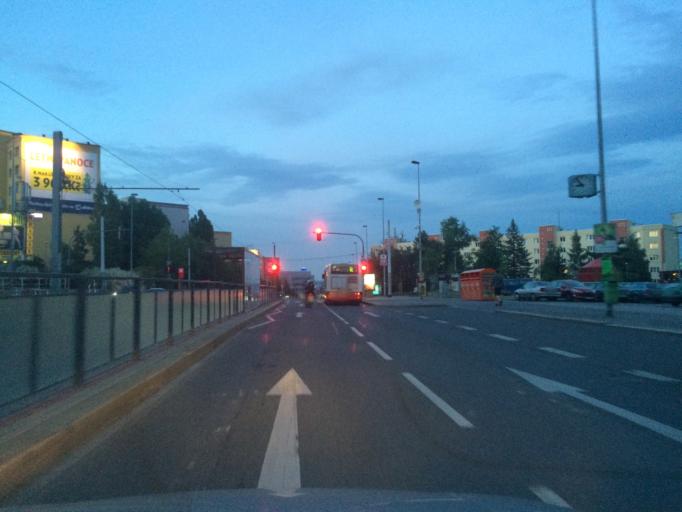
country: CZ
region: Central Bohemia
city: Horomerice
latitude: 50.0978
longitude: 14.3584
